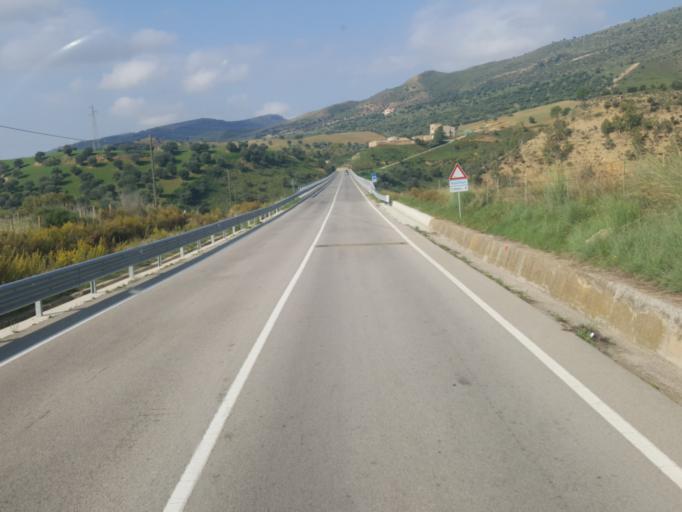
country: IT
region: Sicily
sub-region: Enna
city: Villarosa
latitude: 37.5070
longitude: 14.1742
